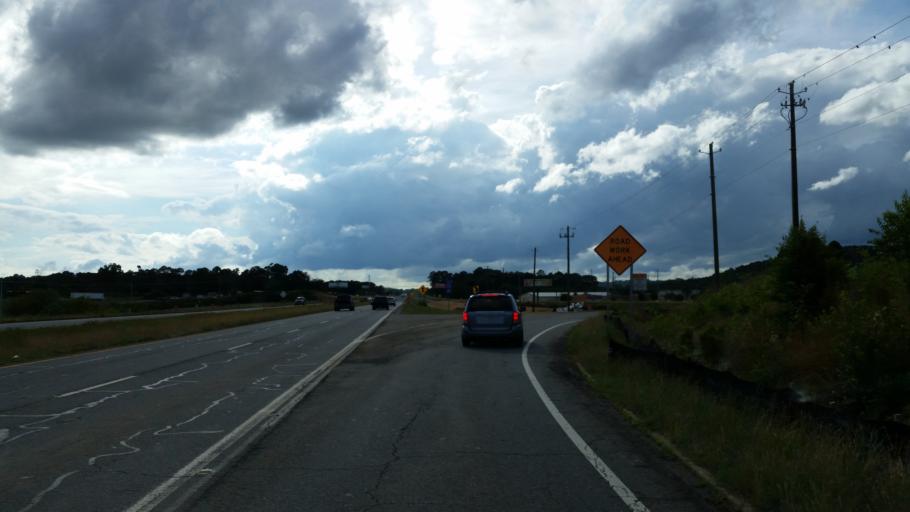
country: US
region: Georgia
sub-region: Bartow County
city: Cartersville
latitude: 34.2000
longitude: -84.7962
